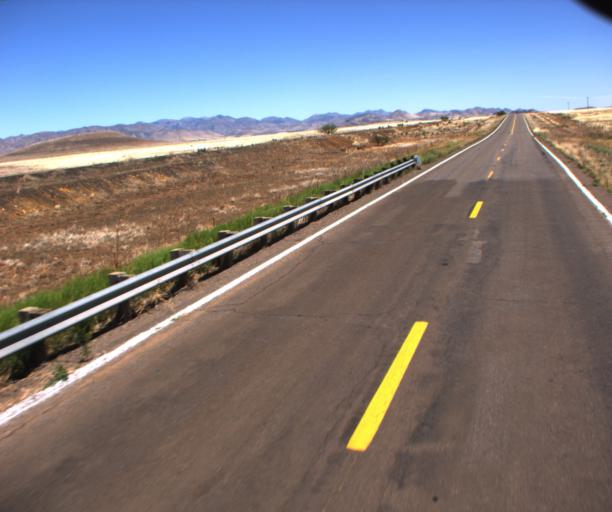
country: US
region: Arizona
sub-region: Cochise County
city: Douglas
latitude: 31.5758
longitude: -109.2571
